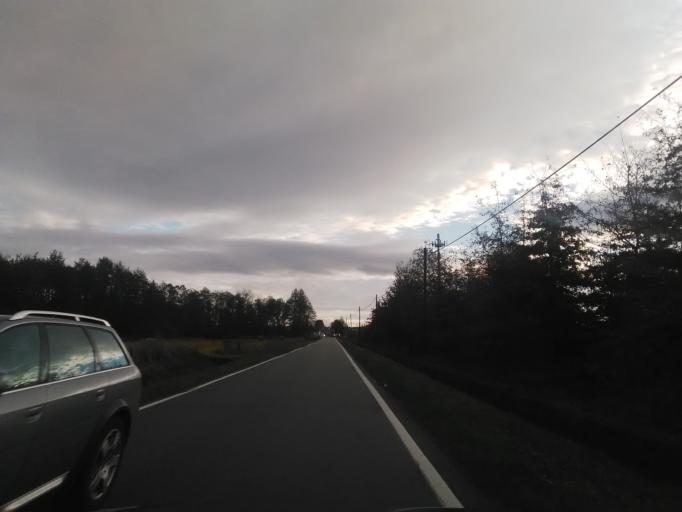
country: IT
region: Piedmont
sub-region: Provincia di Vercelli
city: Lenta
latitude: 45.5556
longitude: 8.3751
